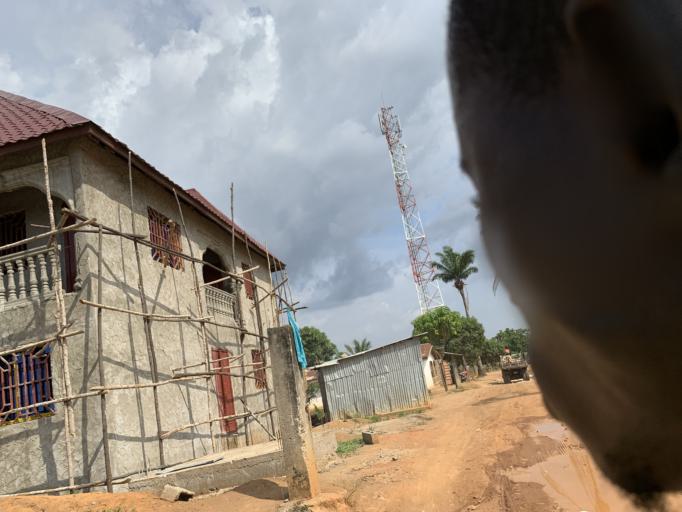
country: SL
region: Western Area
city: Waterloo
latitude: 8.3506
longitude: -13.0428
